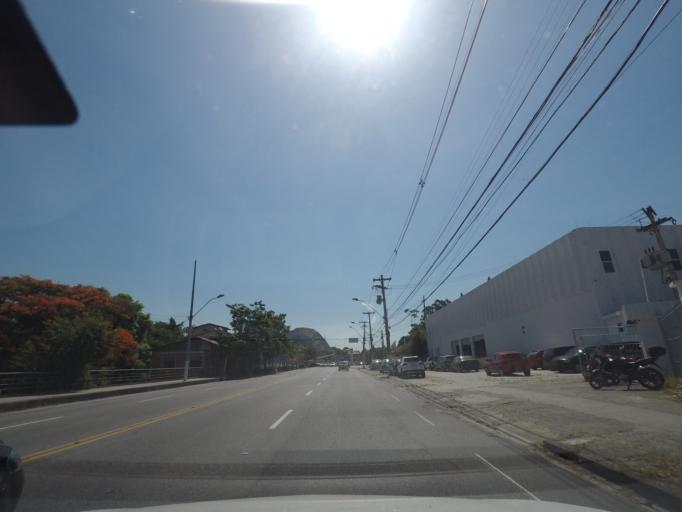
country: BR
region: Rio de Janeiro
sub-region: Niteroi
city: Niteroi
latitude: -22.9115
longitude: -43.0574
